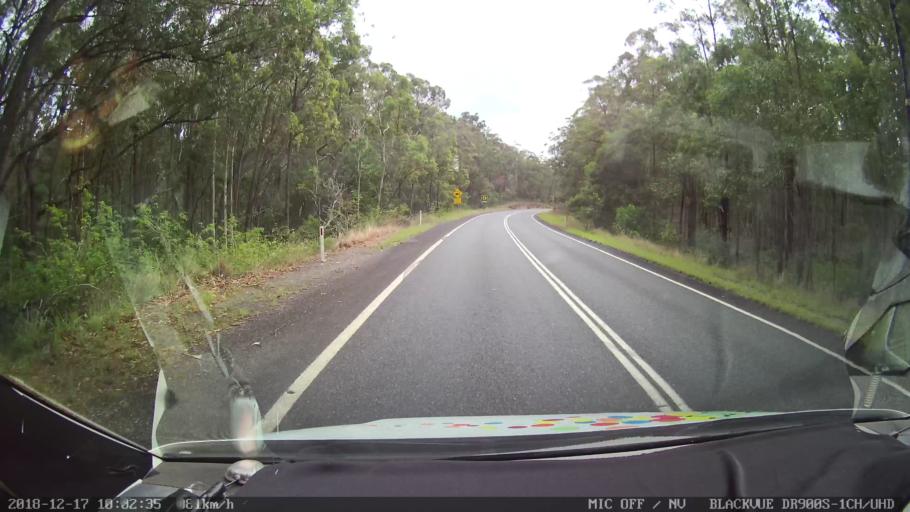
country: AU
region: New South Wales
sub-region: Tenterfield Municipality
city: Carrolls Creek
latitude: -28.9011
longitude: 152.4531
